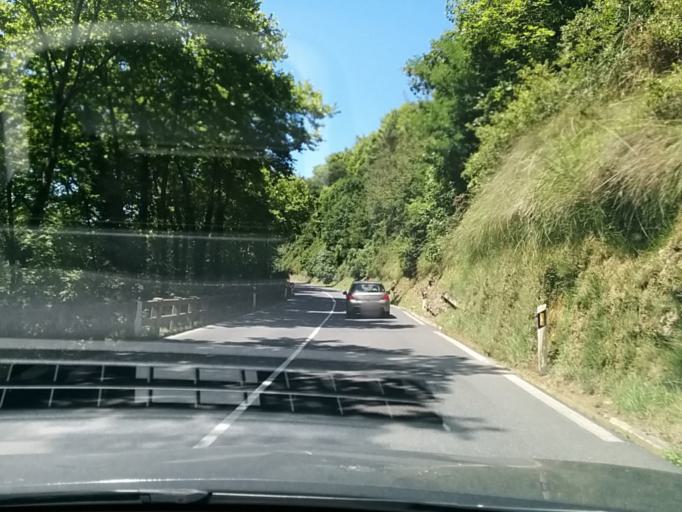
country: ES
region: Basque Country
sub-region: Provincia de Guipuzcoa
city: Usurbil
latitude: 43.2827
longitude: -2.0787
